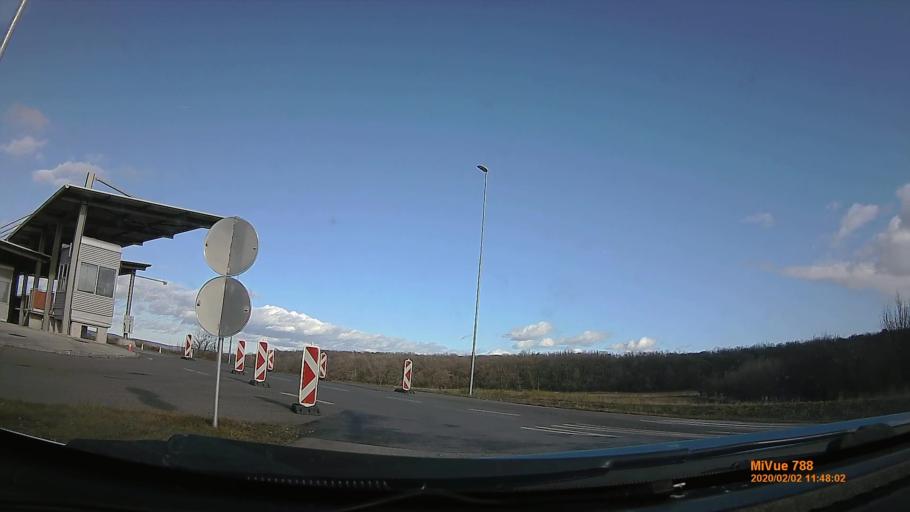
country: AT
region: Burgenland
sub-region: Eisenstadt-Umgebung
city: Klingenbach
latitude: 47.7423
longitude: 16.5450
